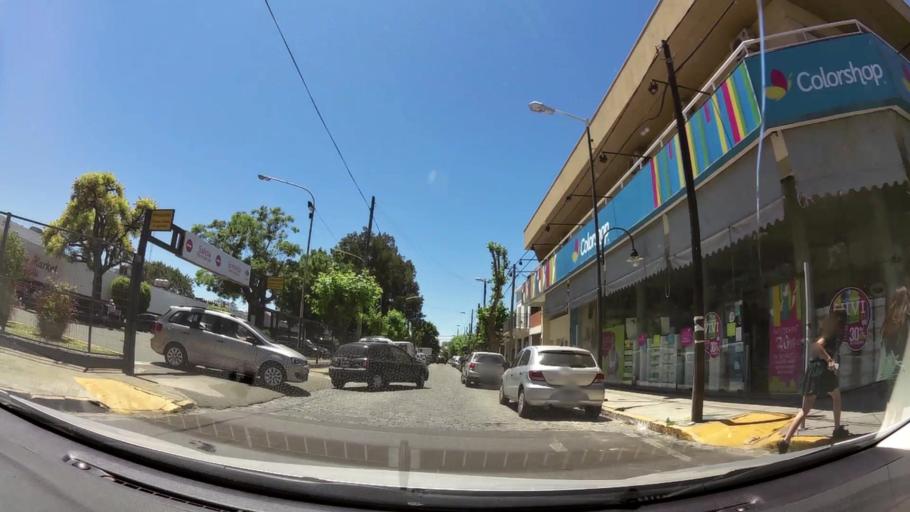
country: AR
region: Buenos Aires
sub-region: Partido de Tigre
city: Tigre
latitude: -34.4423
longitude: -58.5534
